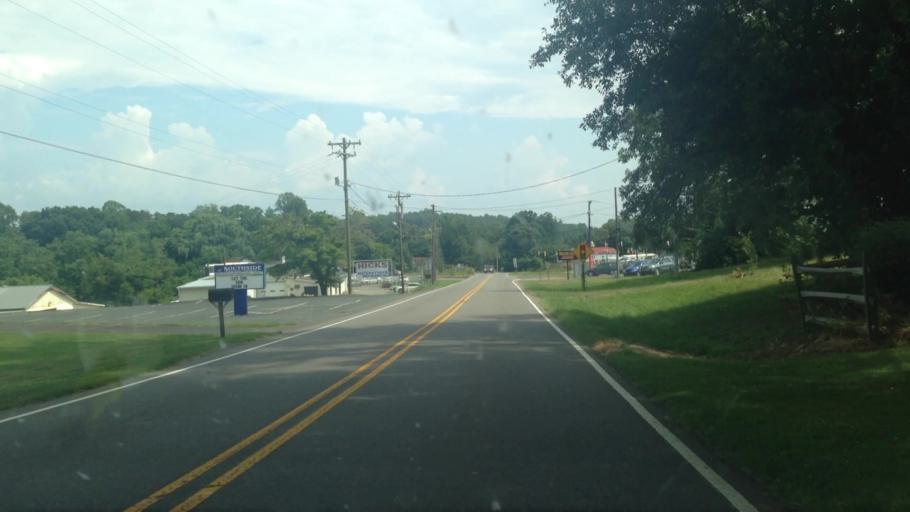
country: US
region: North Carolina
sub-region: Surry County
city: Flat Rock
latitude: 36.4729
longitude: -80.5741
